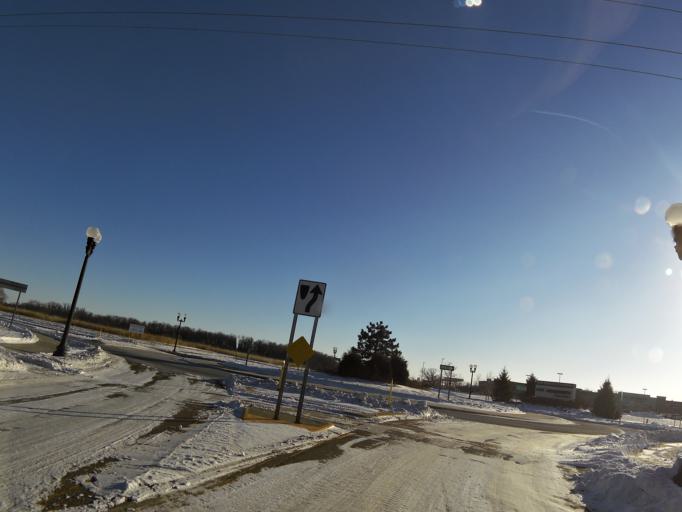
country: US
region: Minnesota
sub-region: Le Sueur County
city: New Prague
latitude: 44.5439
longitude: -93.5530
